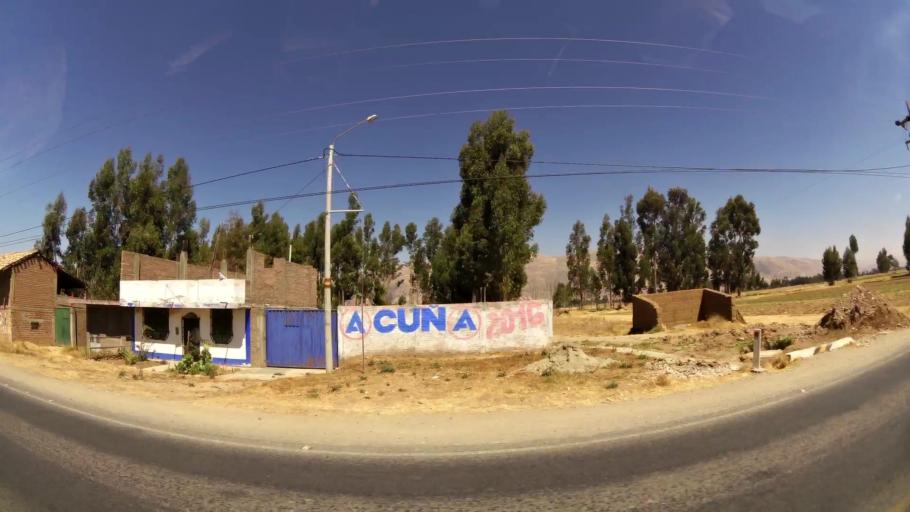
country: PE
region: Junin
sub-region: Provincia de Jauja
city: San Lorenzo
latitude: -11.8425
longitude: -75.3890
